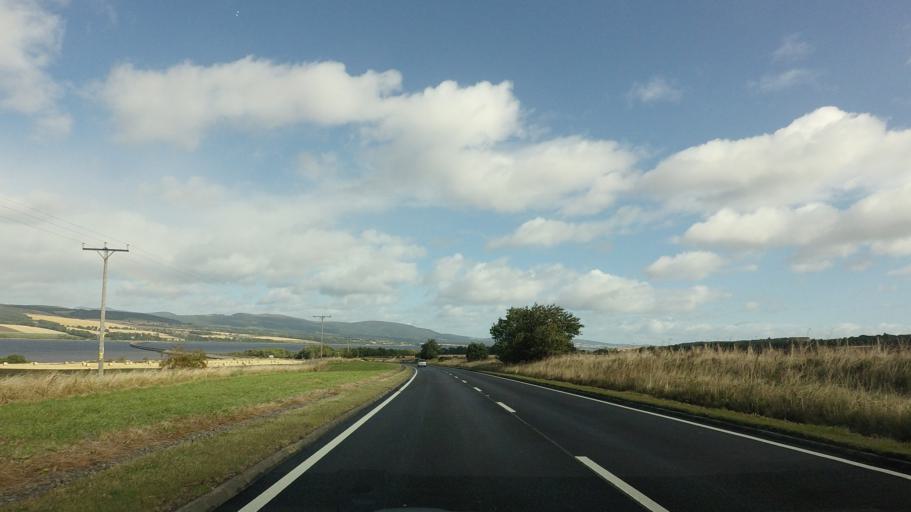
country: GB
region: Scotland
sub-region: Highland
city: Evanton
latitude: 57.6031
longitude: -4.3531
